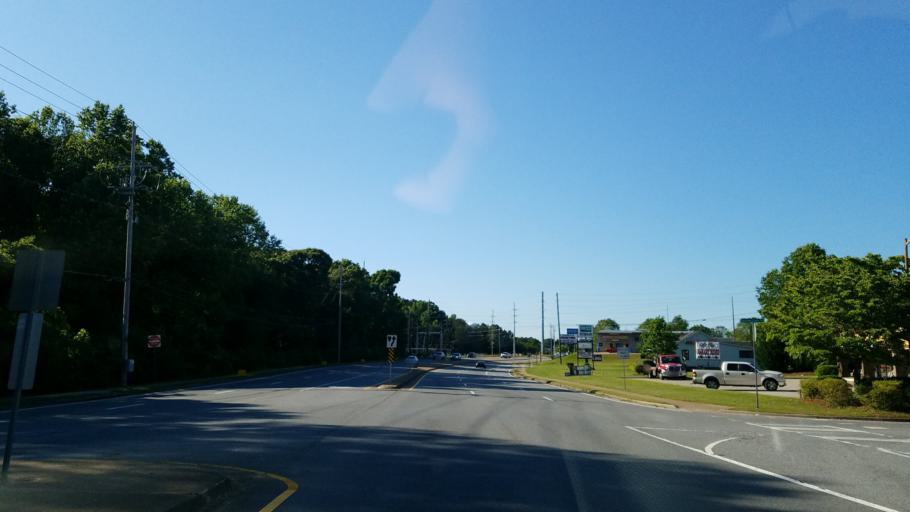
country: US
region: Georgia
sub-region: Cherokee County
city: Woodstock
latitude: 34.1045
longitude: -84.5809
